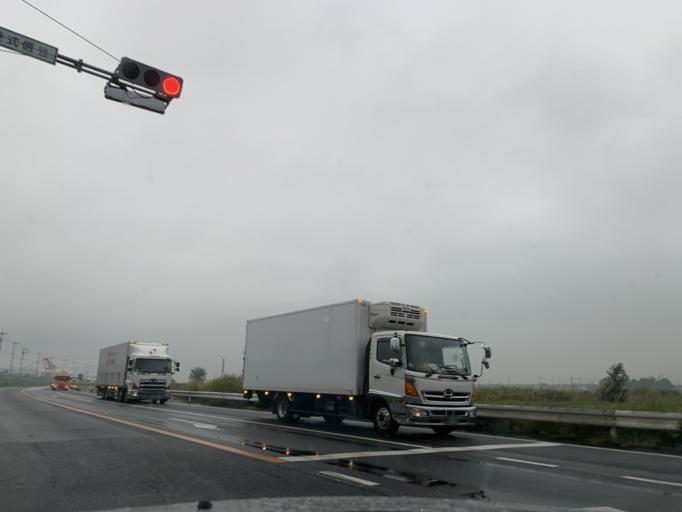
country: JP
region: Chiba
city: Noda
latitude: 35.9087
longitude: 139.8891
